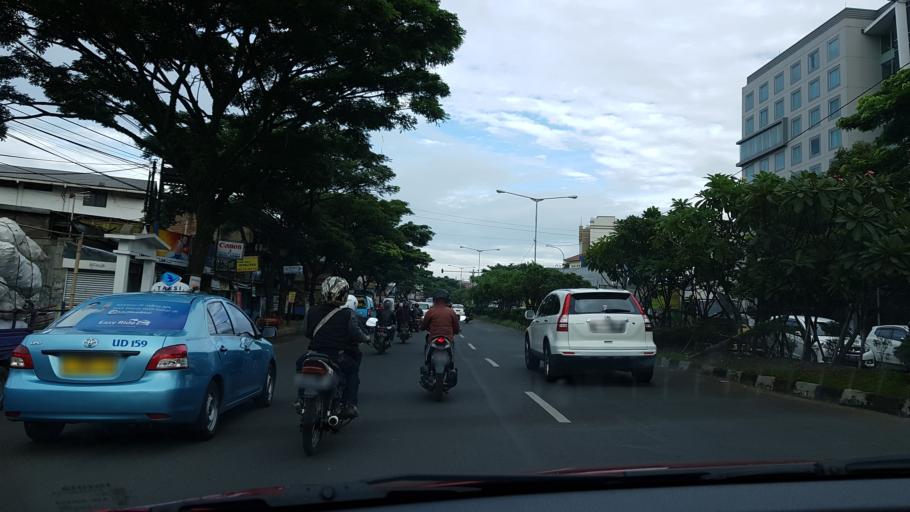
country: ID
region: West Java
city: Bandung
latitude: -6.8968
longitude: 107.5914
